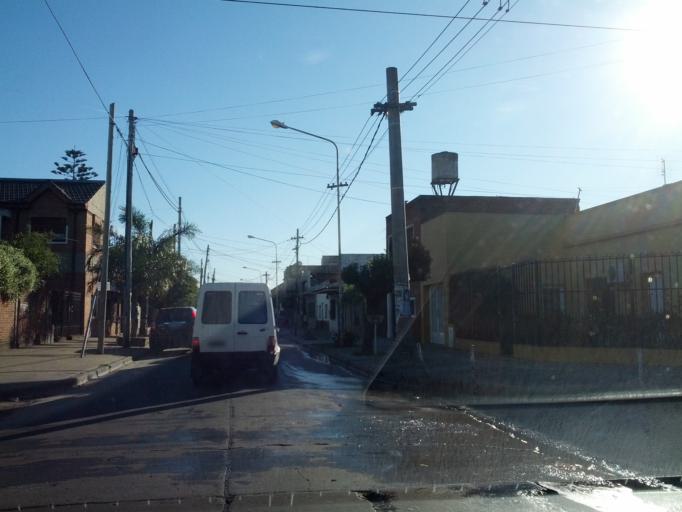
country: AR
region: Buenos Aires
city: San Justo
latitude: -34.6637
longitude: -58.5363
